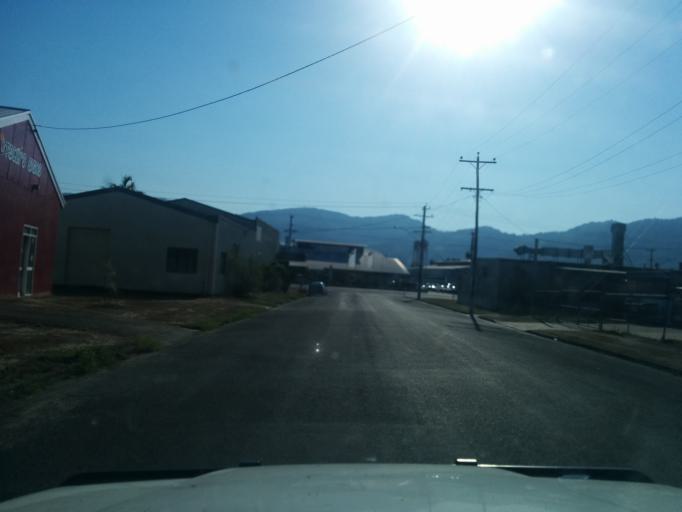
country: AU
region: Queensland
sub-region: Cairns
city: Woree
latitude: -16.9376
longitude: 145.7516
